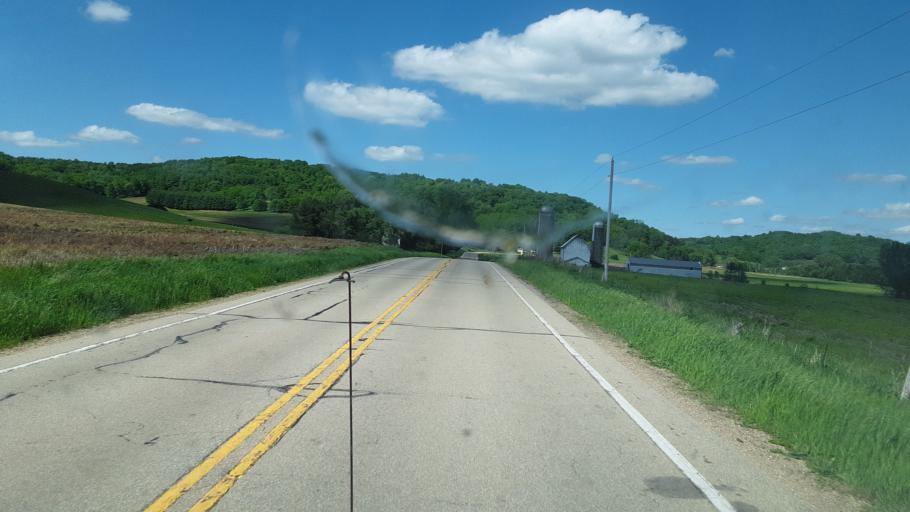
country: US
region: Wisconsin
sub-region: Richland County
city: Richland Center
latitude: 43.4512
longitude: -90.2265
